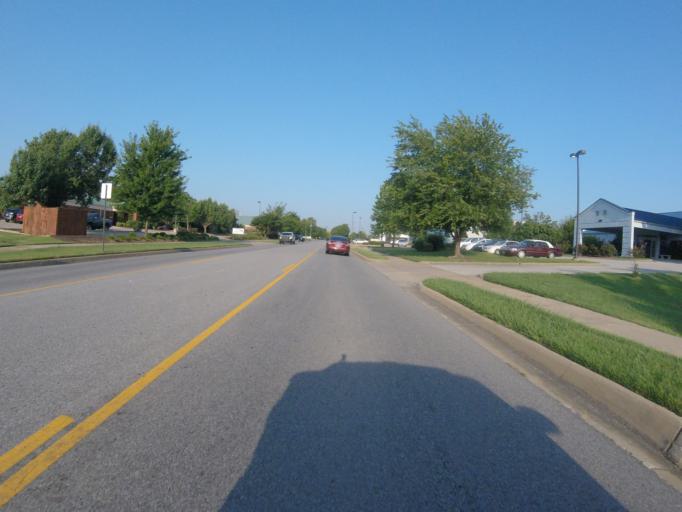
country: US
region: Arkansas
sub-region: Washington County
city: Johnson
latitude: 36.1140
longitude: -94.1517
